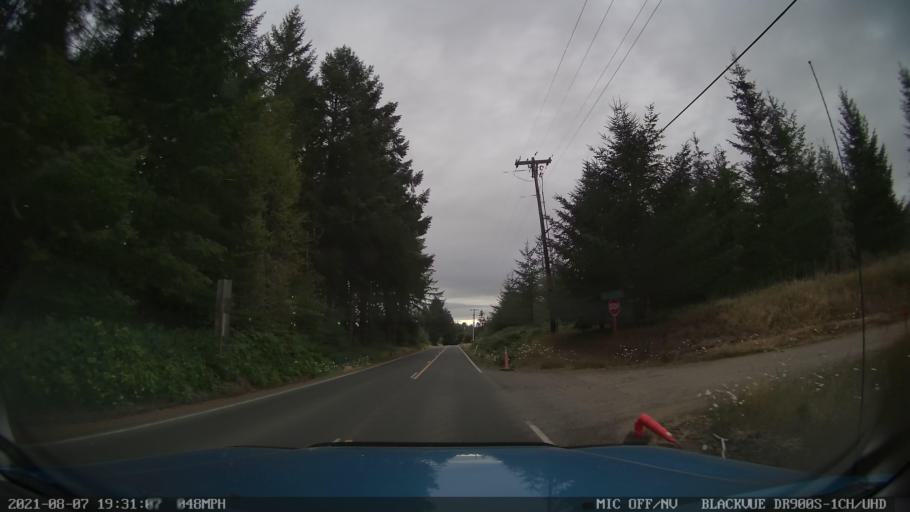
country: US
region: Oregon
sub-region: Linn County
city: Lyons
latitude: 44.8895
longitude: -122.6296
